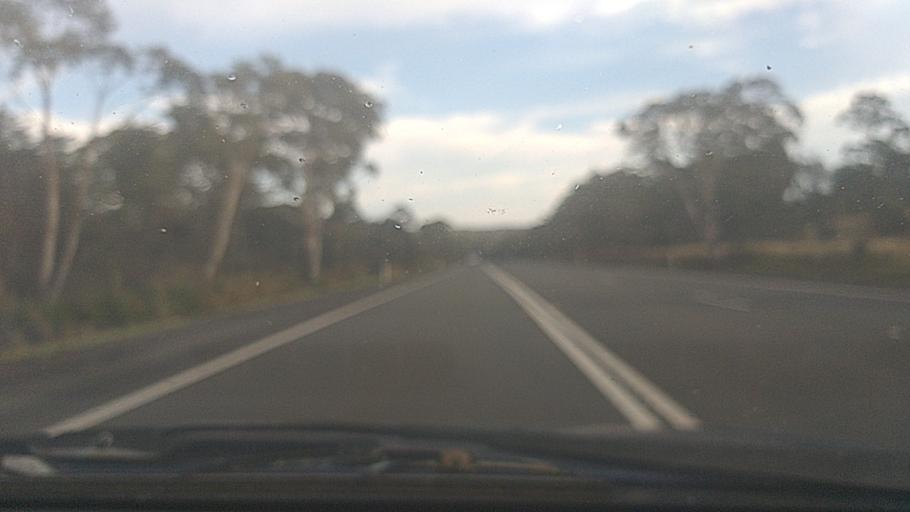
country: AU
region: New South Wales
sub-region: Wollongong
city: Bulli
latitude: -34.2909
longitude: 150.9021
